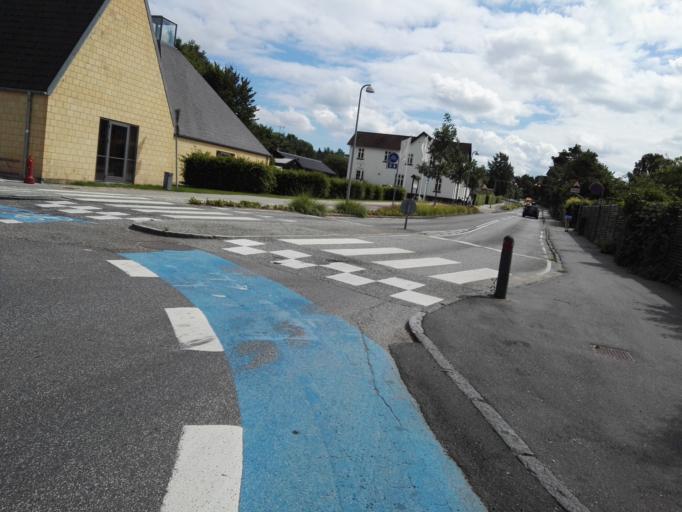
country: DK
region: Capital Region
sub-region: Ballerup Kommune
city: Malov
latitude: 55.7598
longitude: 12.3382
